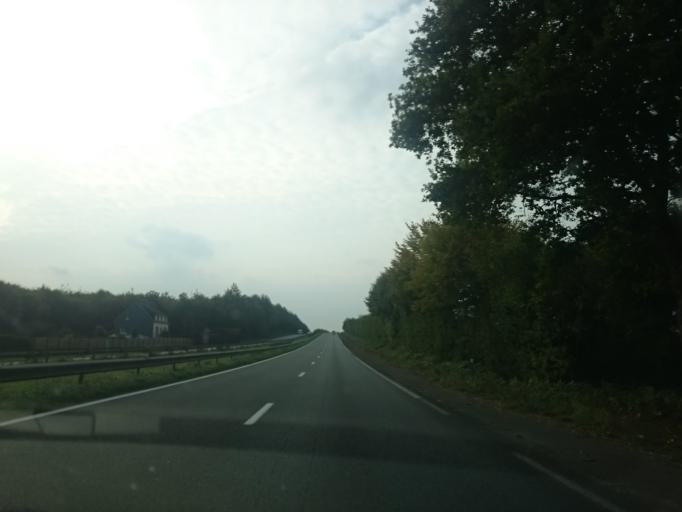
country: FR
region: Brittany
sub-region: Departement des Cotes-d'Armor
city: Graces
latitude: 48.5670
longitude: -3.2300
